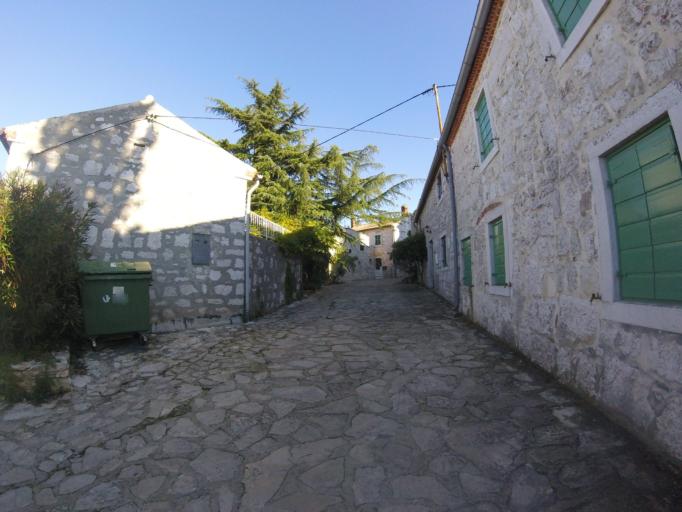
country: HR
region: Istarska
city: Vrsar
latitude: 45.1515
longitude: 13.6065
